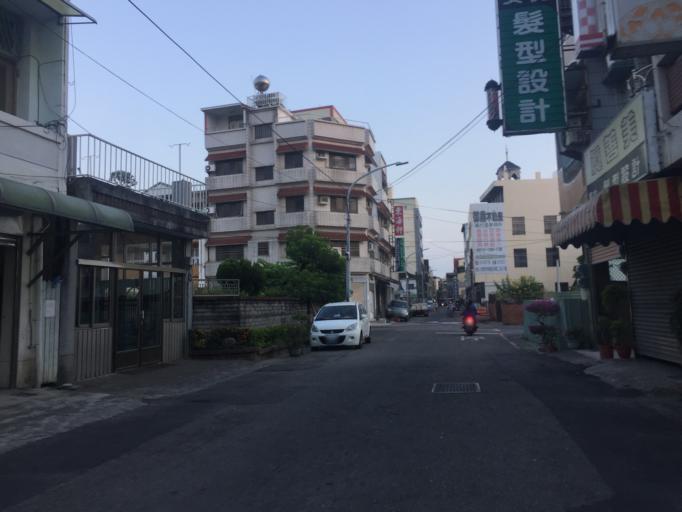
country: TW
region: Taiwan
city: Xinying
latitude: 23.3063
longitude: 120.3134
